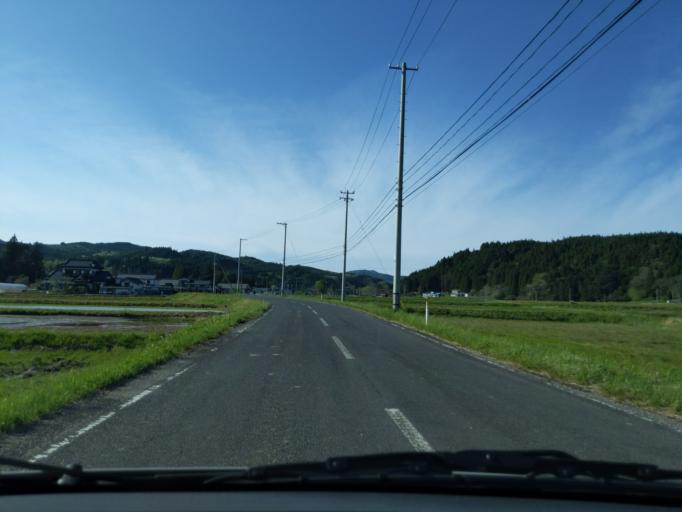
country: JP
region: Iwate
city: Ichinoseki
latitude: 38.8381
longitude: 140.9102
